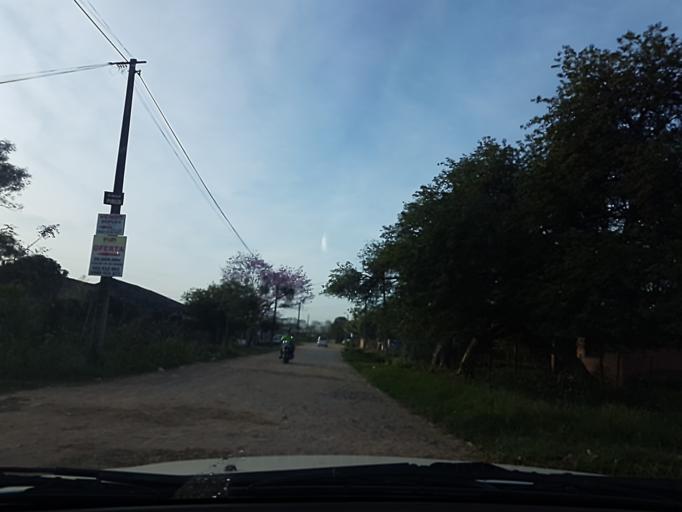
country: PY
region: Central
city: Colonia Mariano Roque Alonso
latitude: -25.2069
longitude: -57.5403
